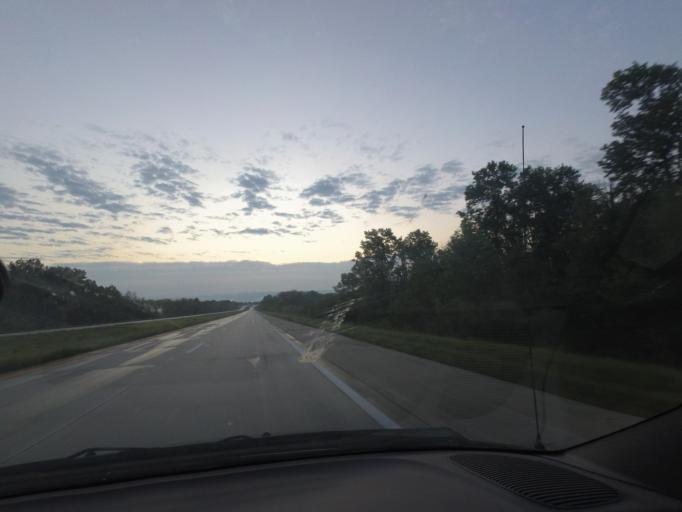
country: US
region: Missouri
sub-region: Macon County
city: Macon
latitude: 39.7590
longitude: -92.5957
